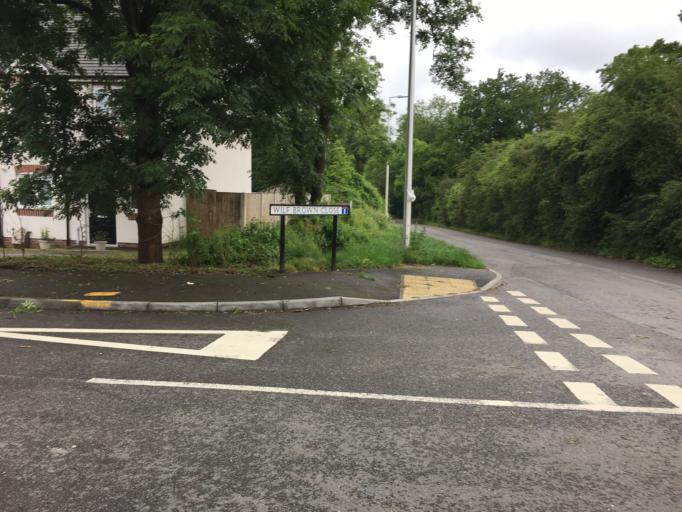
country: GB
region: England
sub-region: Warwickshire
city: Rugby
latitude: 52.3942
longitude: -1.2516
